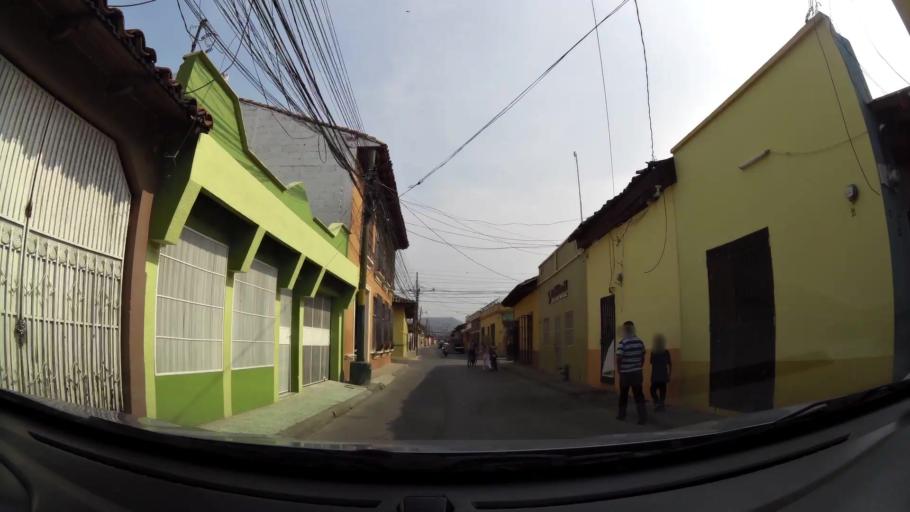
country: HN
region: Comayagua
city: Comayagua
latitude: 14.4567
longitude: -87.6423
